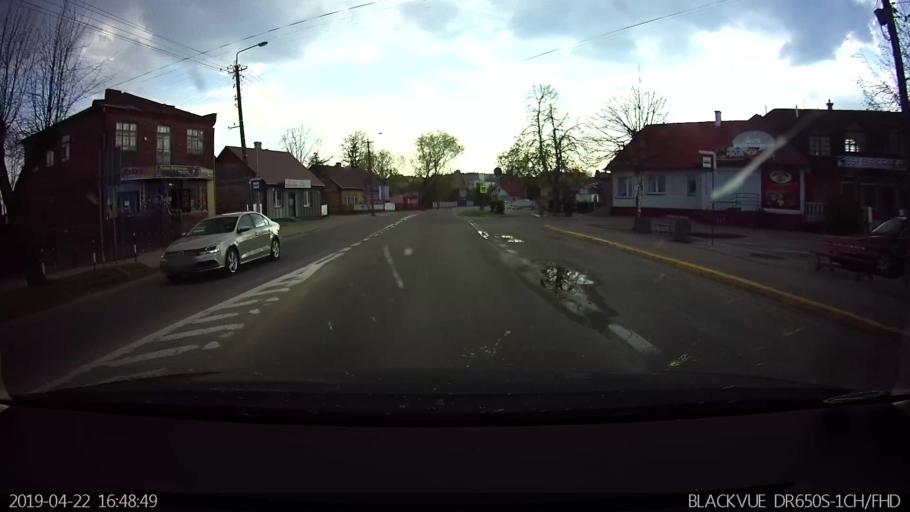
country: PL
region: Podlasie
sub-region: Powiat siemiatycki
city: Siemiatycze
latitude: 52.4278
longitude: 22.8699
